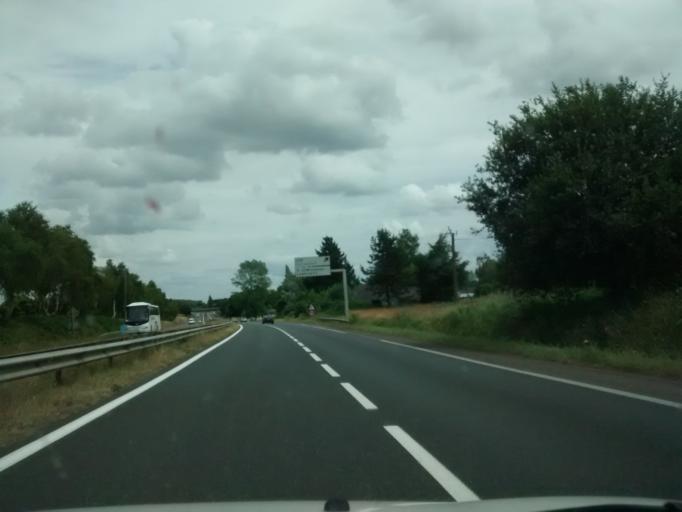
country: FR
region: Brittany
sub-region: Departement des Cotes-d'Armor
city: Lanrodec
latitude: 48.5361
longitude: -3.0527
